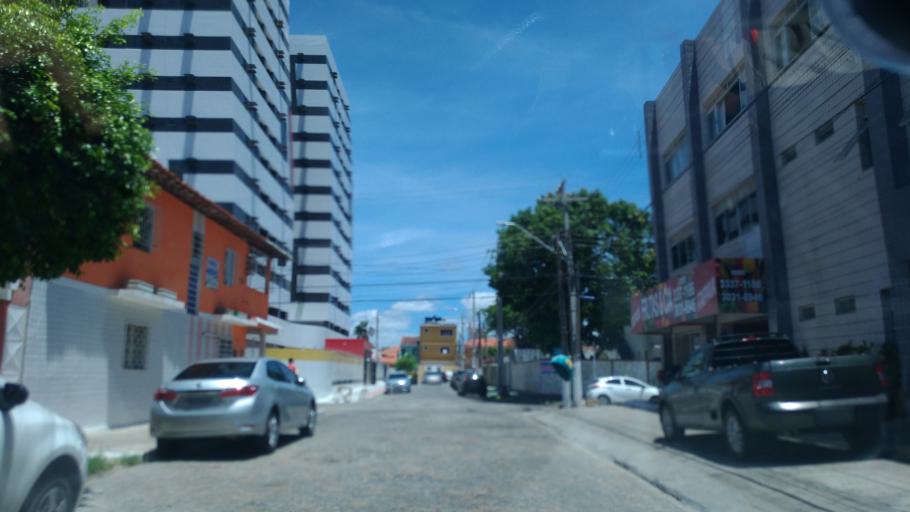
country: BR
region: Alagoas
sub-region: Maceio
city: Maceio
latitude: -9.6600
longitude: -35.7118
